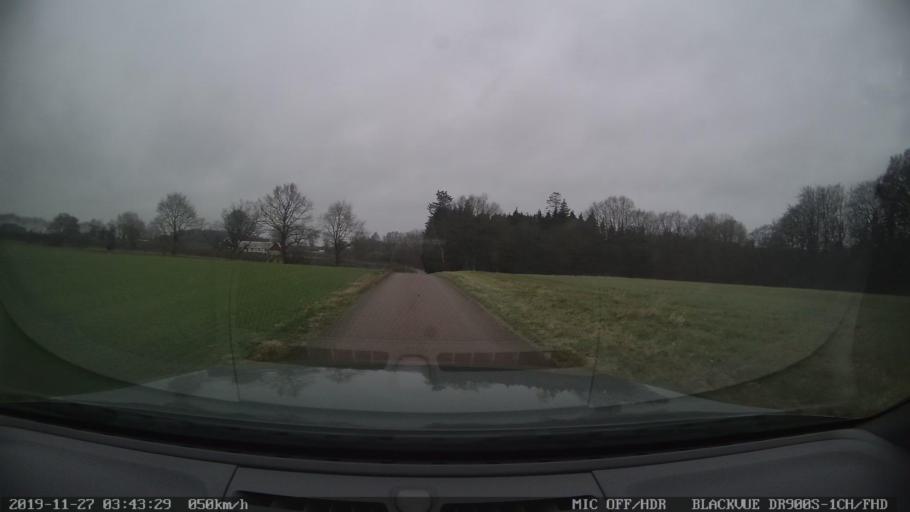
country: SE
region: Skane
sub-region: Hoganas Kommun
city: Hoganas
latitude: 56.2649
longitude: 12.5510
